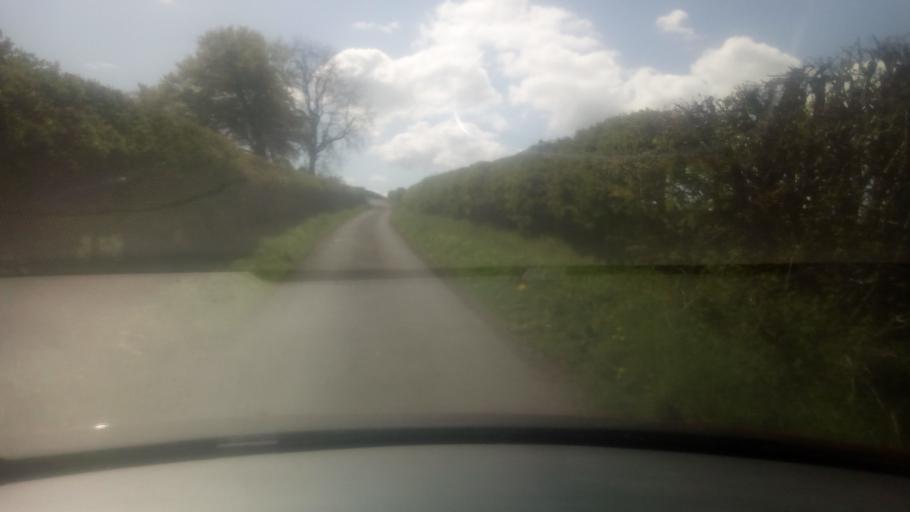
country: GB
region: Scotland
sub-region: The Scottish Borders
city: Hawick
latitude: 55.4206
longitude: -2.7172
